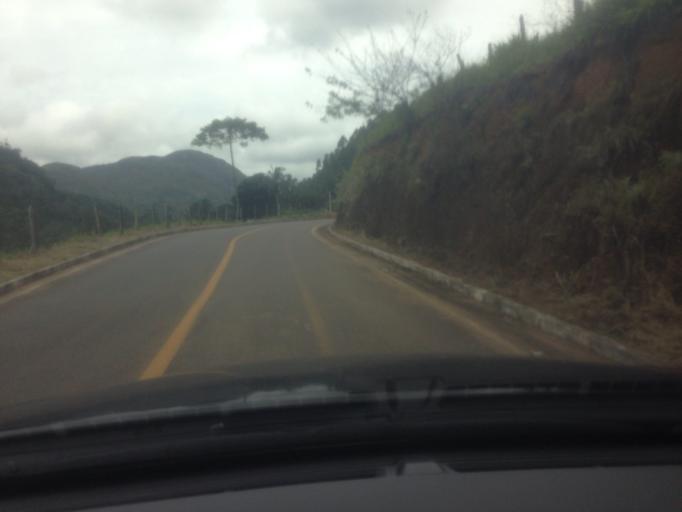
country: BR
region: Espirito Santo
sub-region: Guarapari
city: Guarapari
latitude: -20.5653
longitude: -40.5486
